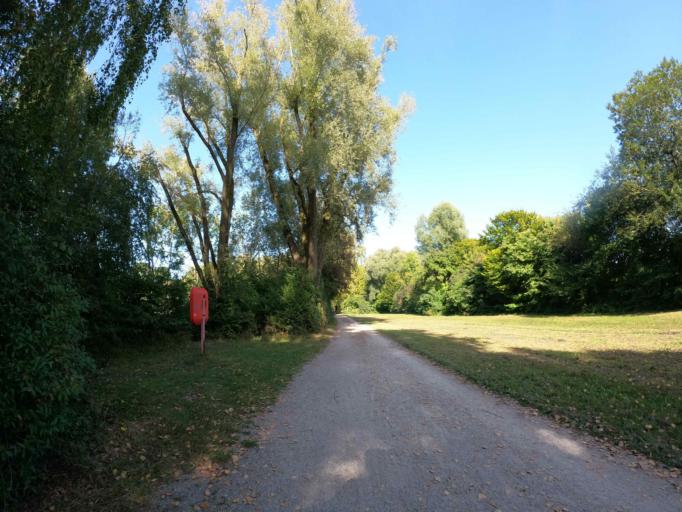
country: DE
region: Bavaria
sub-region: Upper Bavaria
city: Karlsfeld
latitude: 48.2249
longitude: 11.4401
